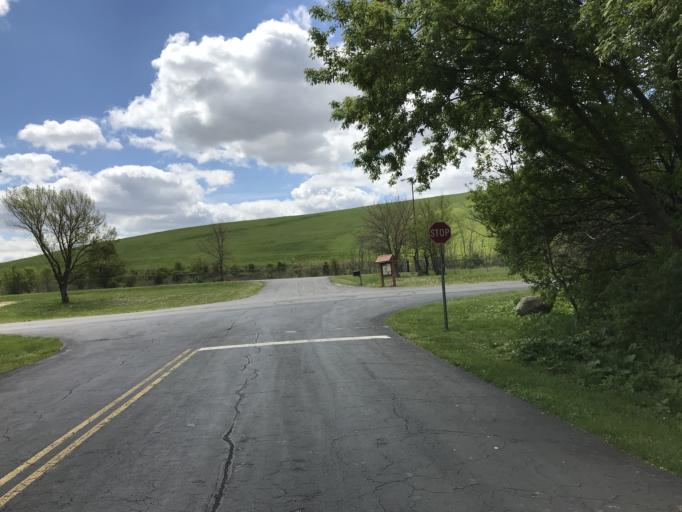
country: US
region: Illinois
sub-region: DuPage County
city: Woodridge
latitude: 41.7366
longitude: -88.0748
